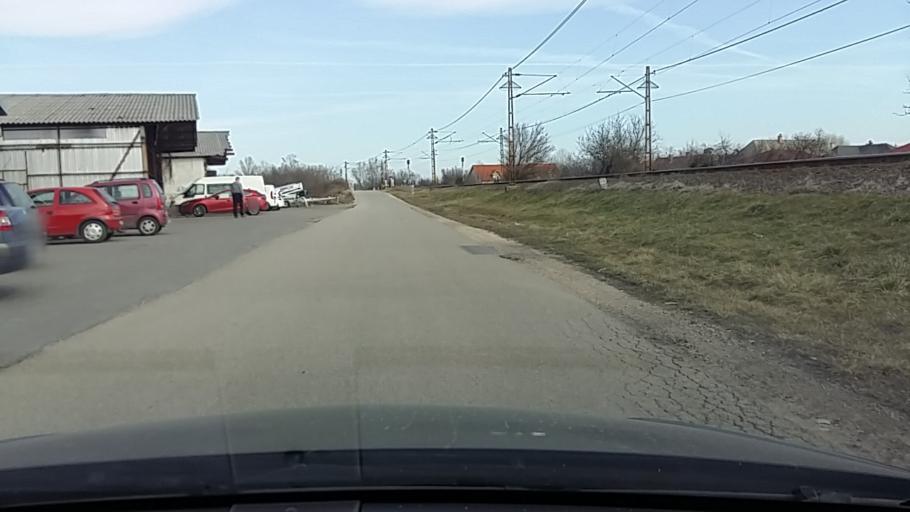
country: HU
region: Pest
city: Szigetszentmiklos
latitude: 47.3524
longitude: 19.0635
